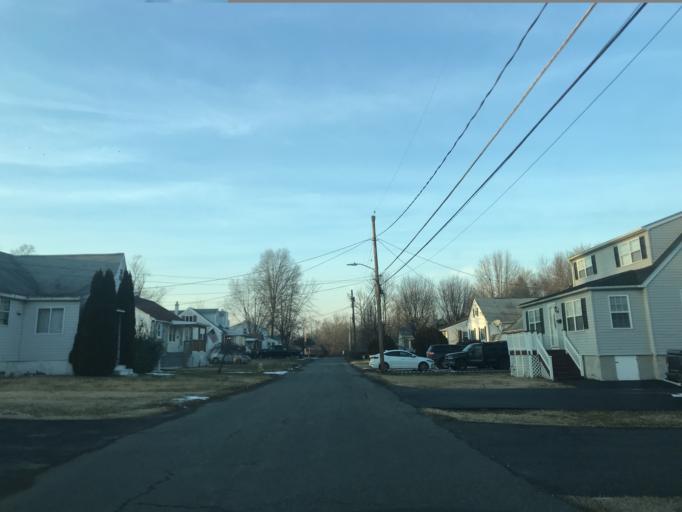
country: US
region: Maryland
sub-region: Harford County
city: Edgewood
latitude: 39.4206
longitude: -76.2920
